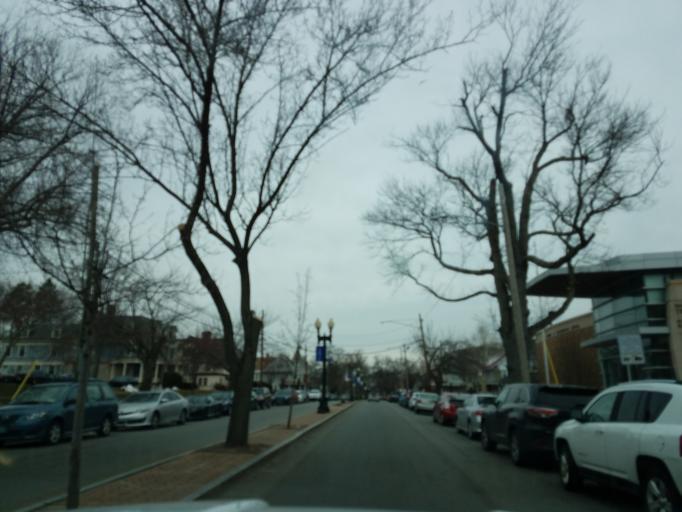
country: US
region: Connecticut
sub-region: Fairfield County
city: Bridgeport
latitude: 41.1656
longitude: -73.1915
